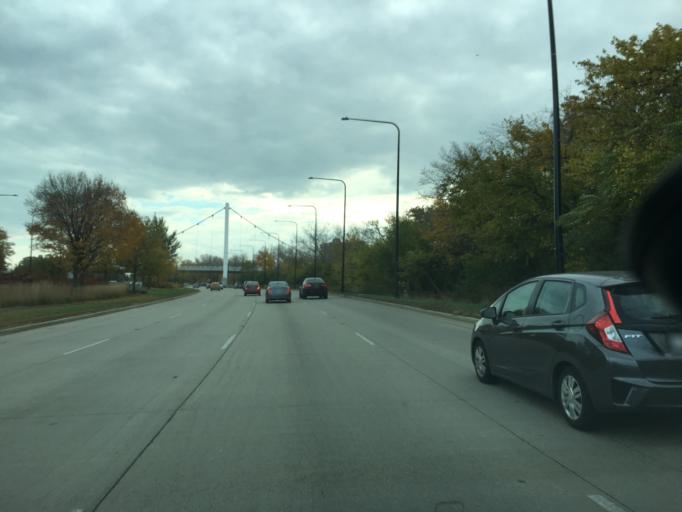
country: US
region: Illinois
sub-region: Cook County
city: Chicago
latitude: 41.8338
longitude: -87.6079
